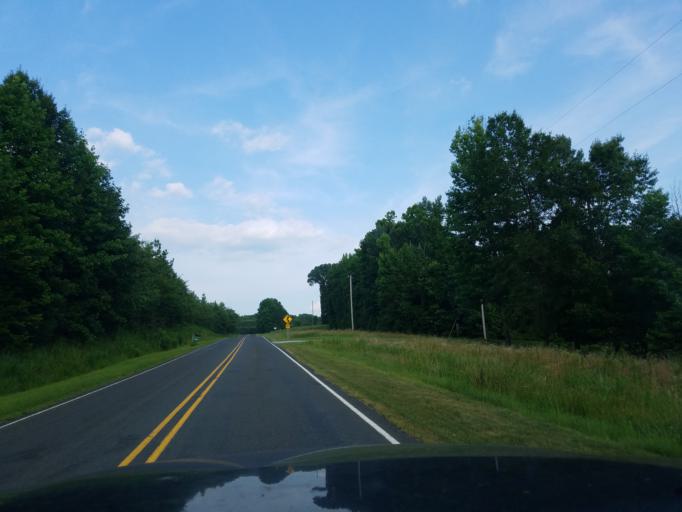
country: US
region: North Carolina
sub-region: Granville County
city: Butner
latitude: 36.2164
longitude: -78.8742
